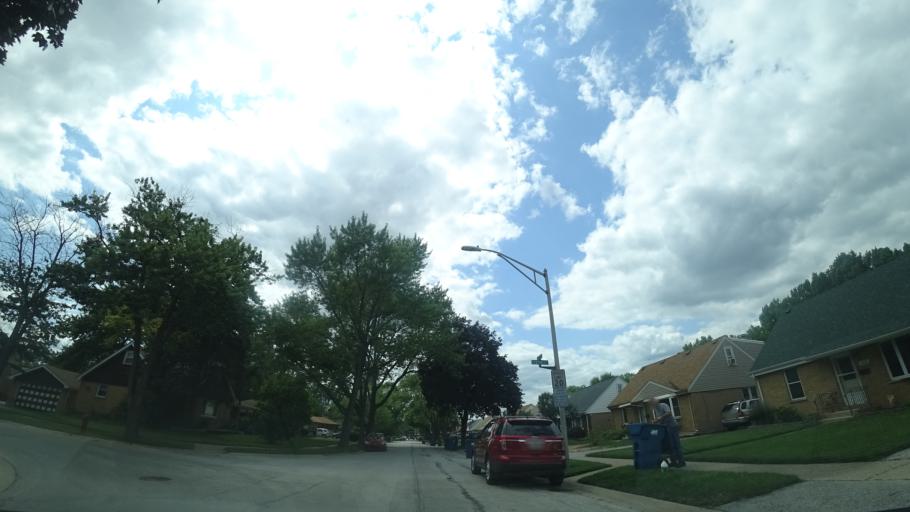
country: US
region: Illinois
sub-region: Cook County
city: Alsip
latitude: 41.6831
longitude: -87.7335
